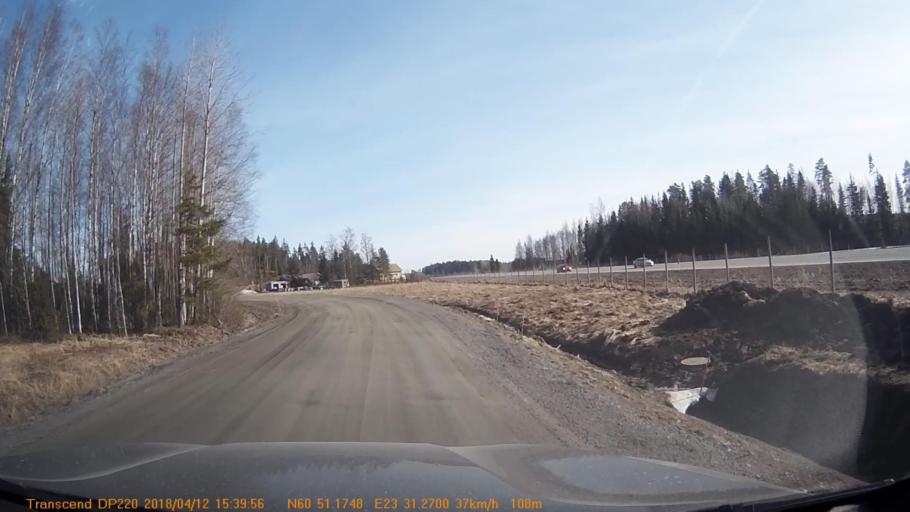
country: FI
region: Haeme
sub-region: Forssa
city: Jokioinen
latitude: 60.8527
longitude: 23.5214
